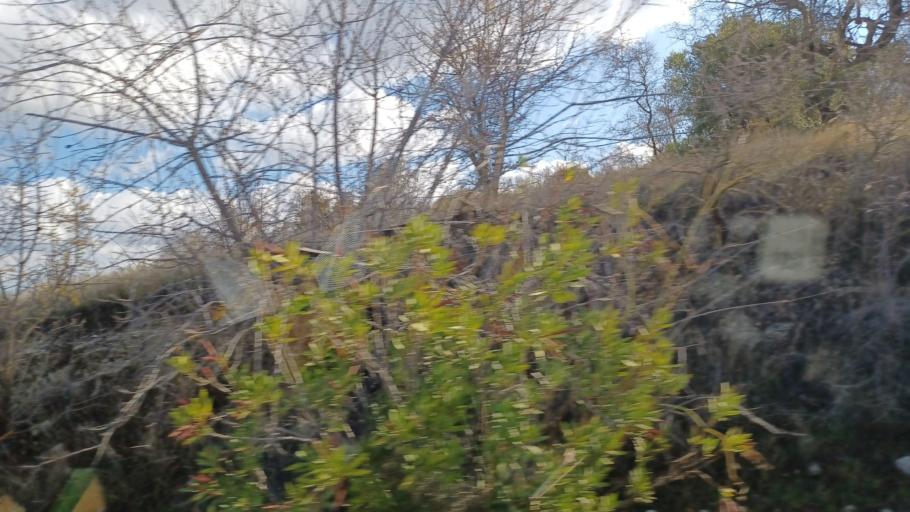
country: CY
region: Limassol
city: Pachna
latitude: 34.8321
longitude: 32.6845
